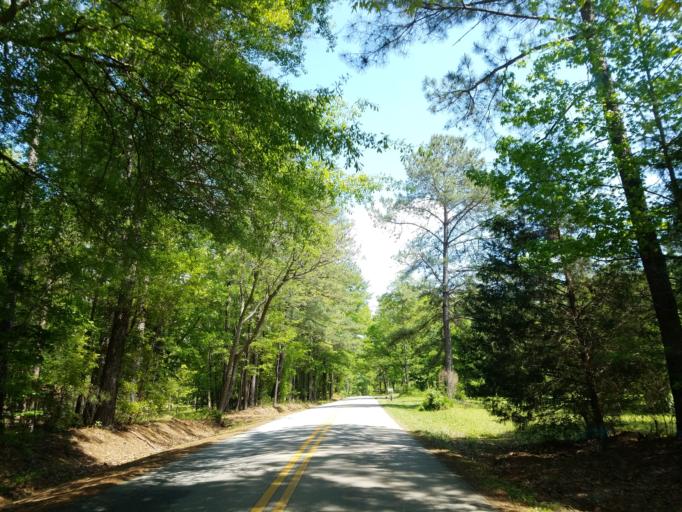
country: US
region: Georgia
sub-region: Monroe County
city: Forsyth
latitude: 33.1389
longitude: -83.9816
